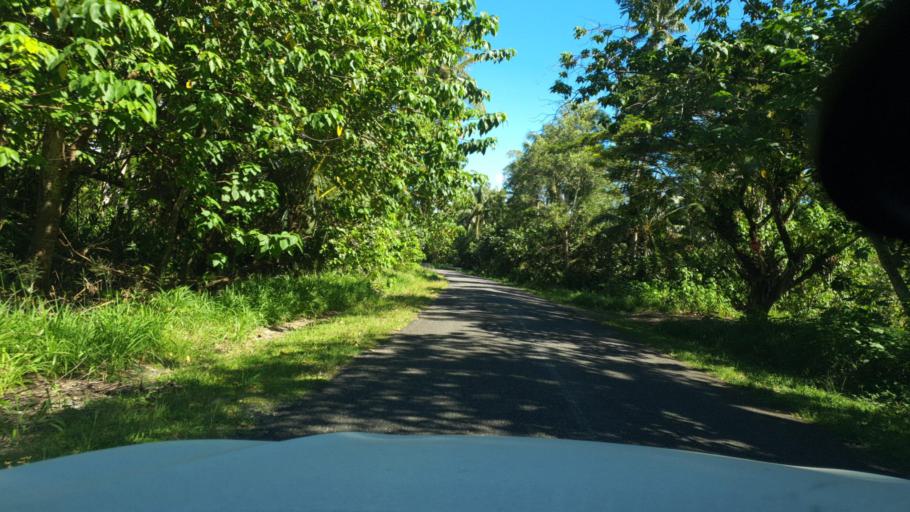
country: SB
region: Guadalcanal
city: Honiara
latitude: -9.2939
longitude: 159.7759
